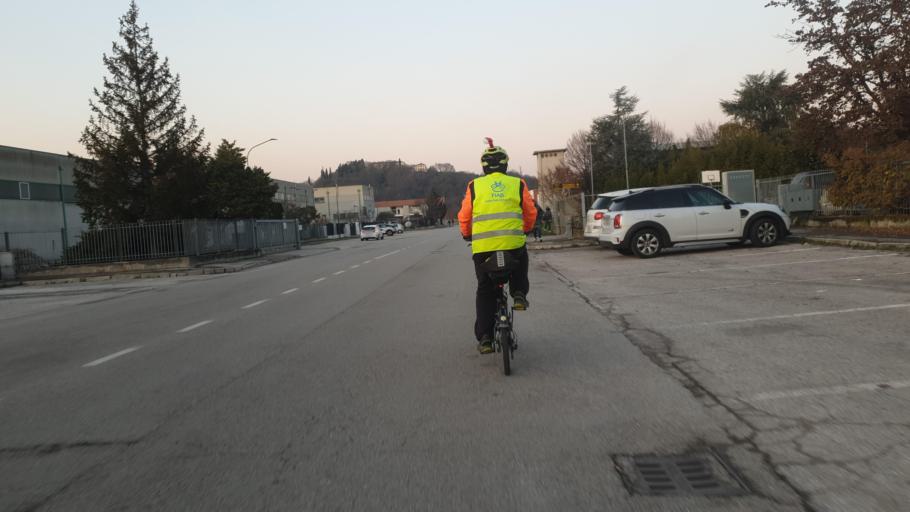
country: IT
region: Veneto
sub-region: Provincia di Padova
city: Montegrotto Terme
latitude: 45.3367
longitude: 11.7655
